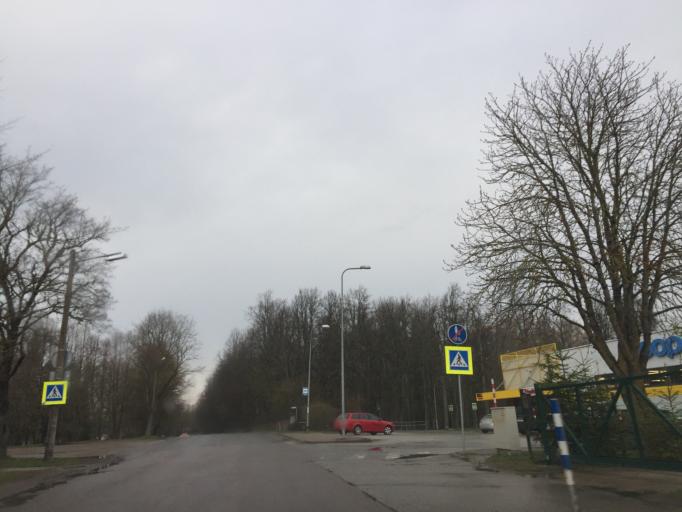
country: EE
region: Tartu
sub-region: UElenurme vald
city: Ulenurme
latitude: 58.3146
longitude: 26.7214
